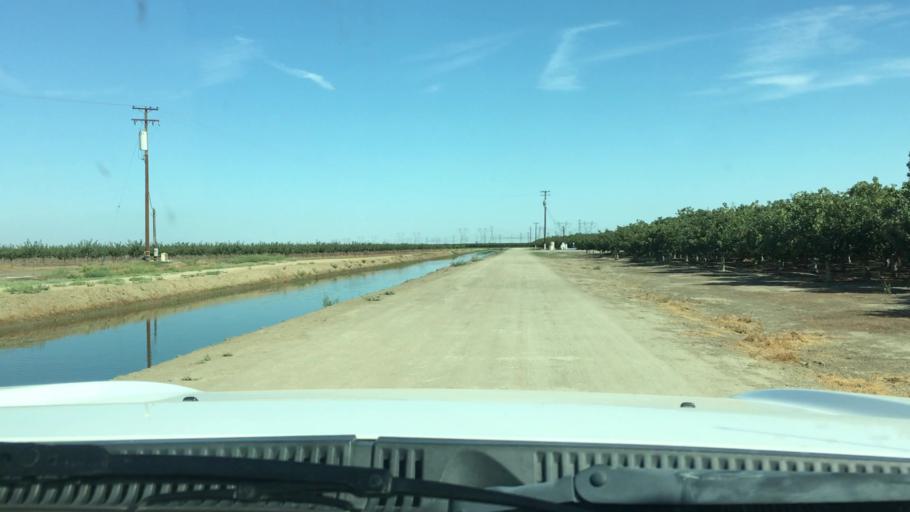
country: US
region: California
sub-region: Kern County
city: Buttonwillow
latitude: 35.3714
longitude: -119.4001
